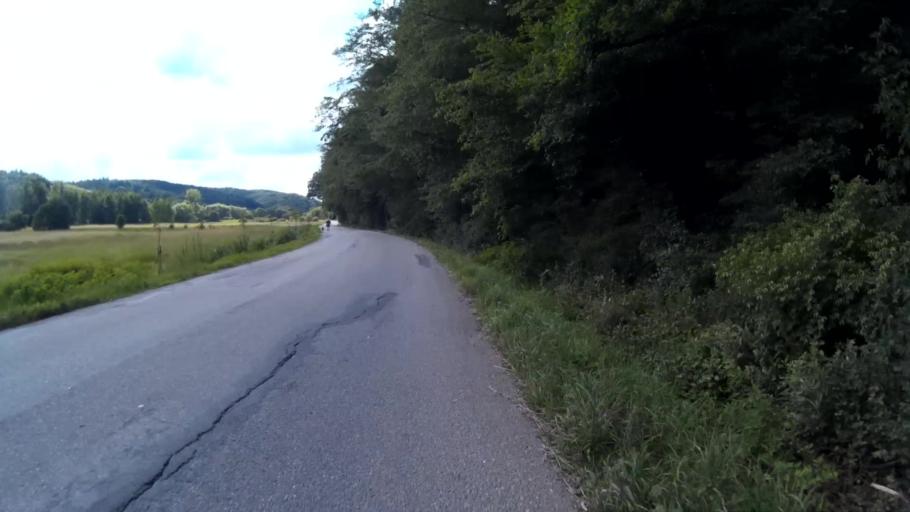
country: CZ
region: South Moravian
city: Strelice
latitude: 49.1525
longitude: 16.4593
